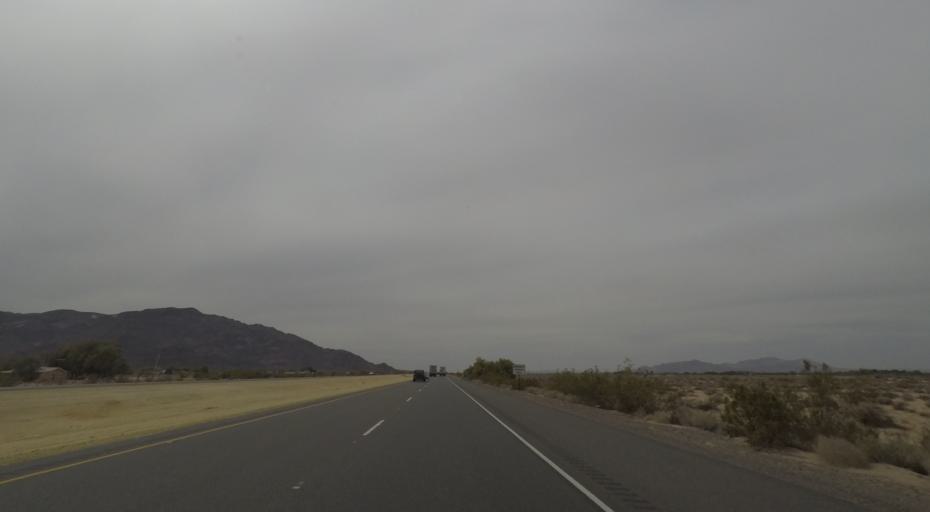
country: US
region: California
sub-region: San Bernardino County
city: Barstow
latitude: 34.8202
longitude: -116.6305
